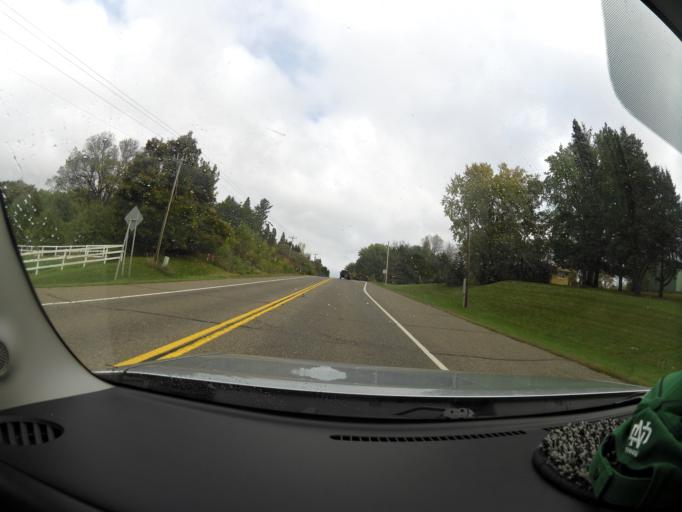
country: US
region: Minnesota
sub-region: Washington County
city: Lake Elmo
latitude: 44.9258
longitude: -92.8626
